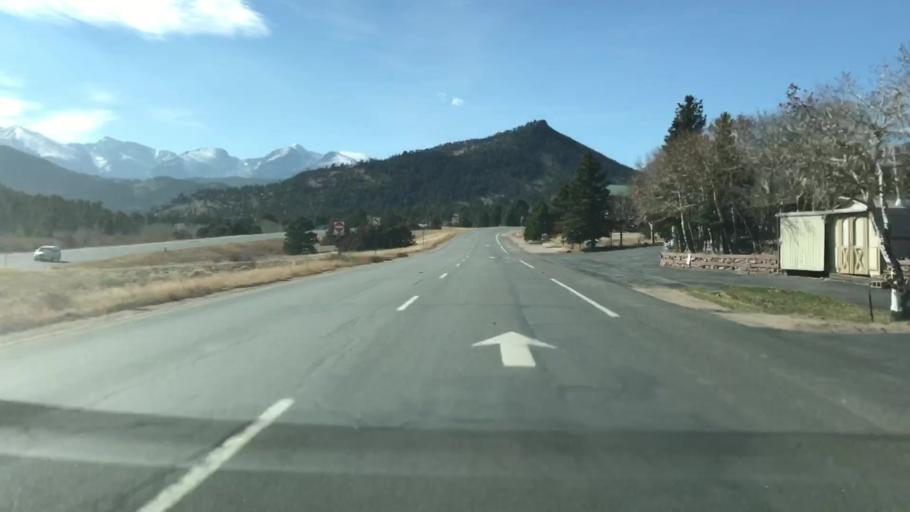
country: US
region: Colorado
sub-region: Larimer County
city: Estes Park
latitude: 40.3639
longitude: -105.5461
